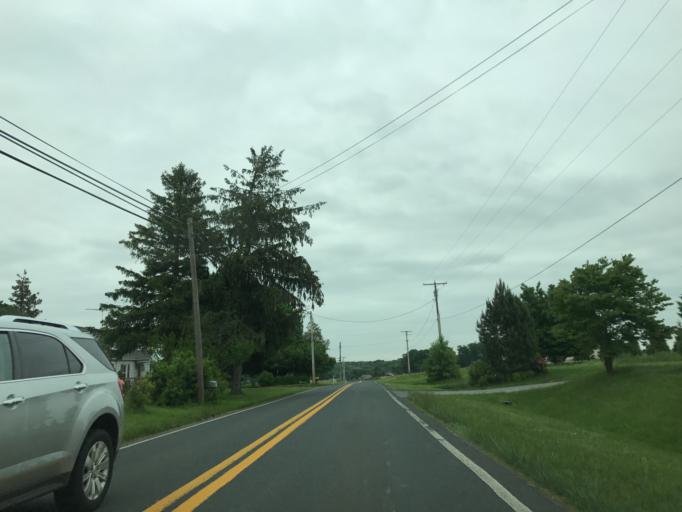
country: US
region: Maryland
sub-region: Carroll County
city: Hampstead
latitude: 39.6166
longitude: -76.8394
